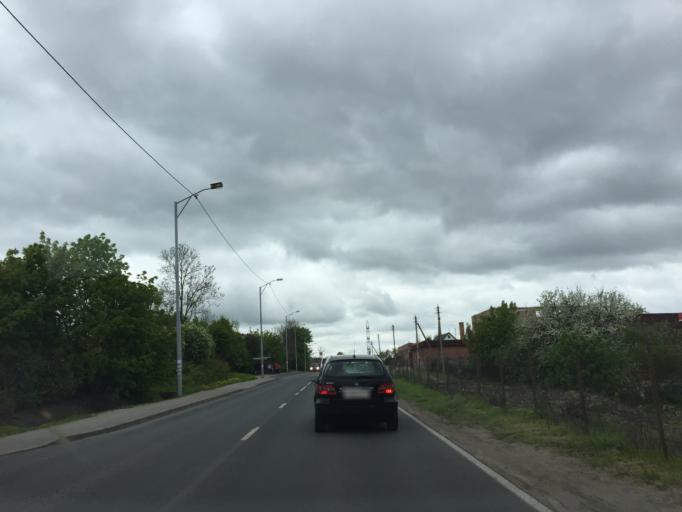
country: RU
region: Kaliningrad
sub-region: Gorod Kaliningrad
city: Kaliningrad
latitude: 54.6730
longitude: 20.4363
